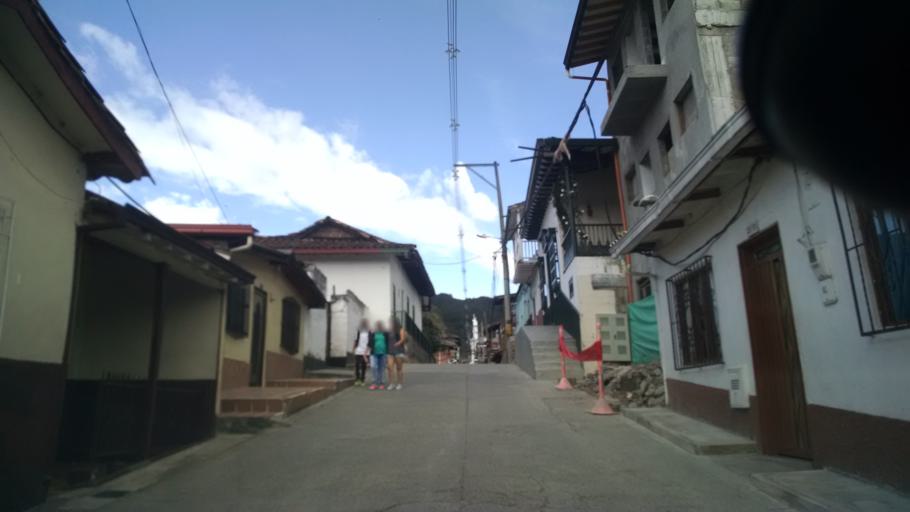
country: CO
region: Antioquia
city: El Retiro
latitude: 6.0567
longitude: -75.5047
